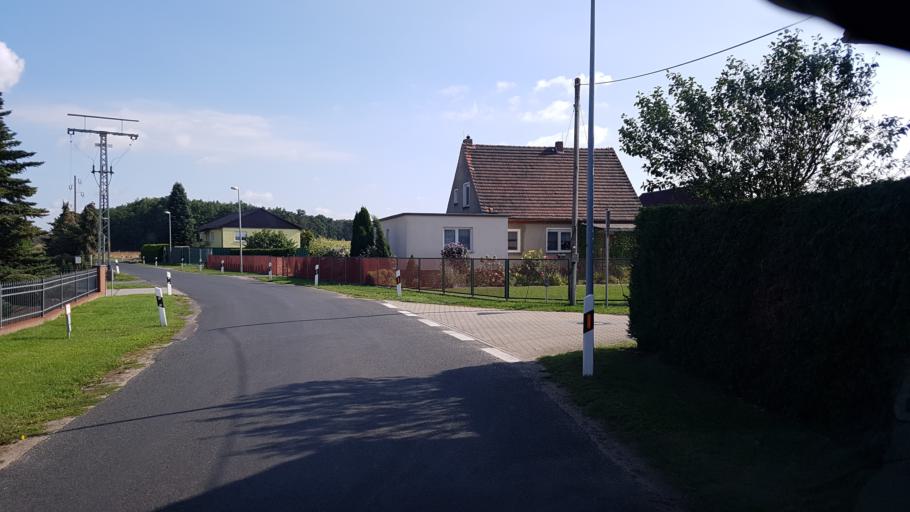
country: DE
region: Brandenburg
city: Luebben
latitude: 51.8708
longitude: 13.8803
